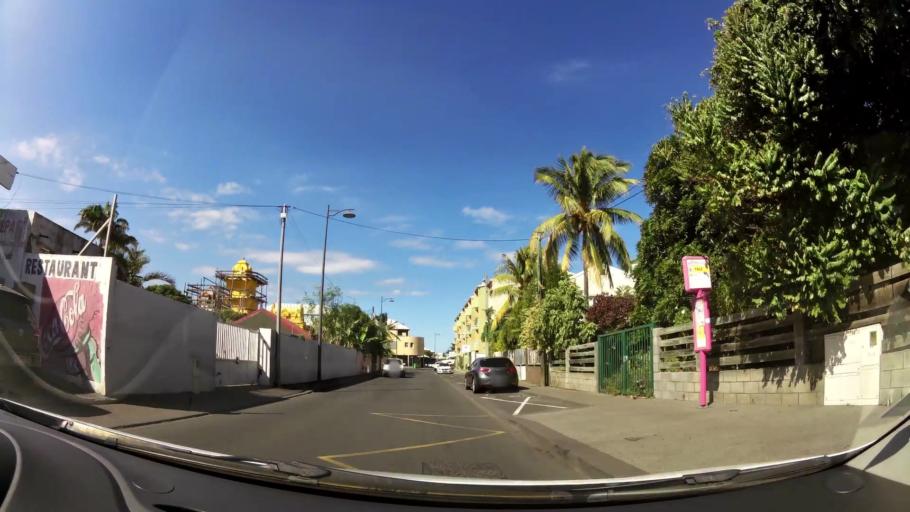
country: RE
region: Reunion
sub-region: Reunion
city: Saint-Pierre
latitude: -21.3372
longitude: 55.4596
